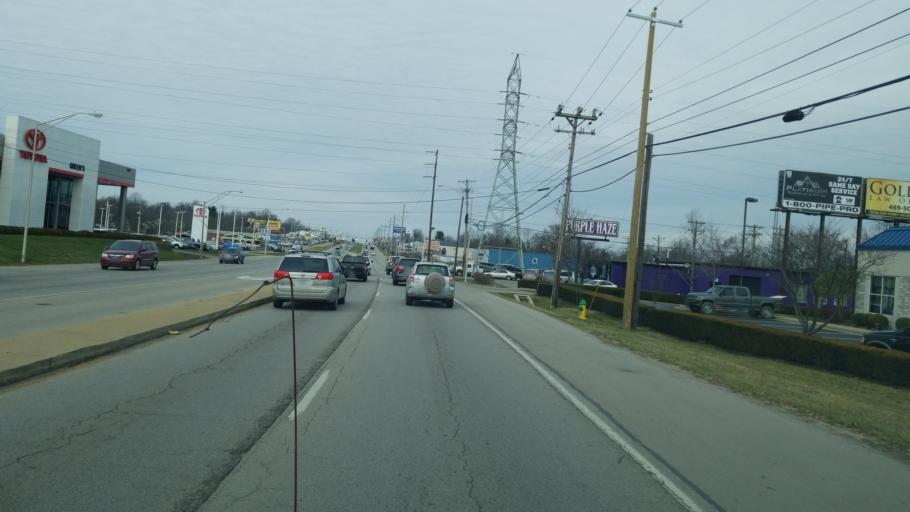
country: US
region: Kentucky
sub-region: Fayette County
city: Lexington-Fayette
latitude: 38.0500
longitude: -84.4552
